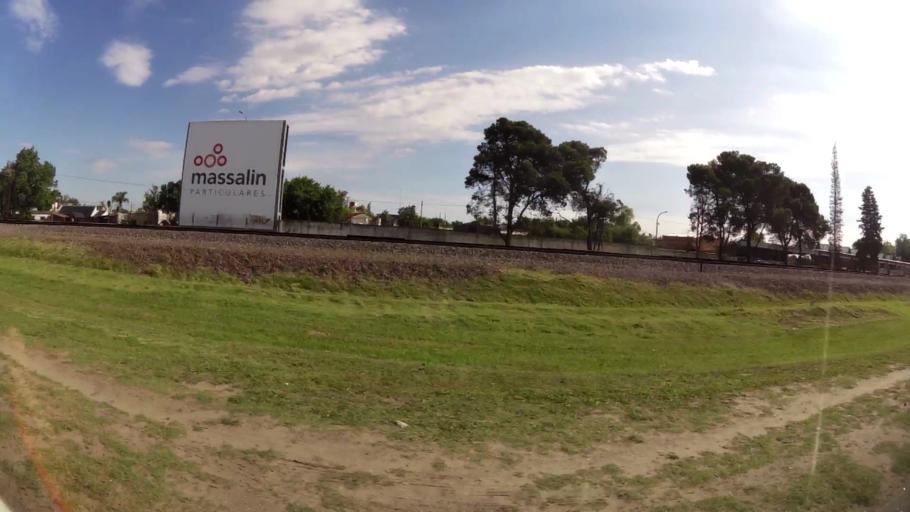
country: AR
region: Buenos Aires
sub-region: Partido de Merlo
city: Merlo
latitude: -34.6622
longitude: -58.7410
